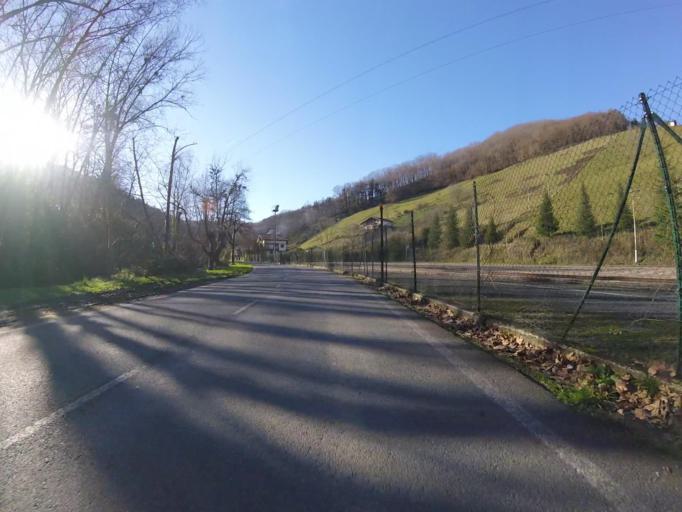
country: ES
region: Navarre
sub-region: Provincia de Navarra
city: Lesaka
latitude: 43.2478
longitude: -1.7142
